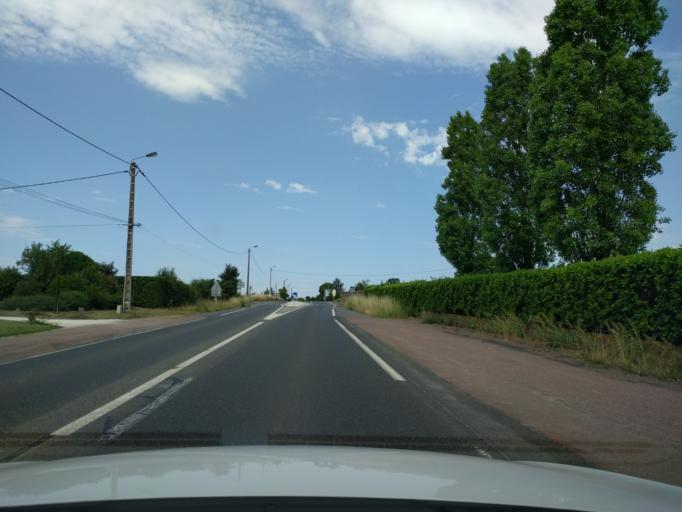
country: FR
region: Poitou-Charentes
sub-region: Departement des Deux-Sevres
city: Bessines
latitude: 46.3473
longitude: -0.5075
